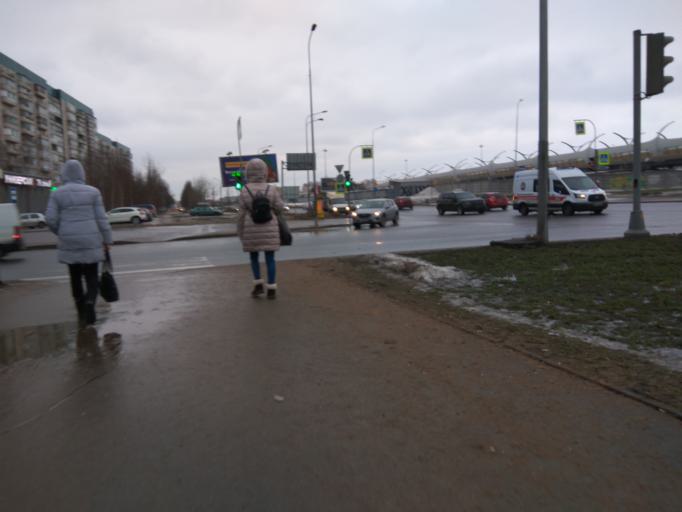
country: RU
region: St.-Petersburg
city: Staraya Derevnya
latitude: 60.0037
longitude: 30.2357
